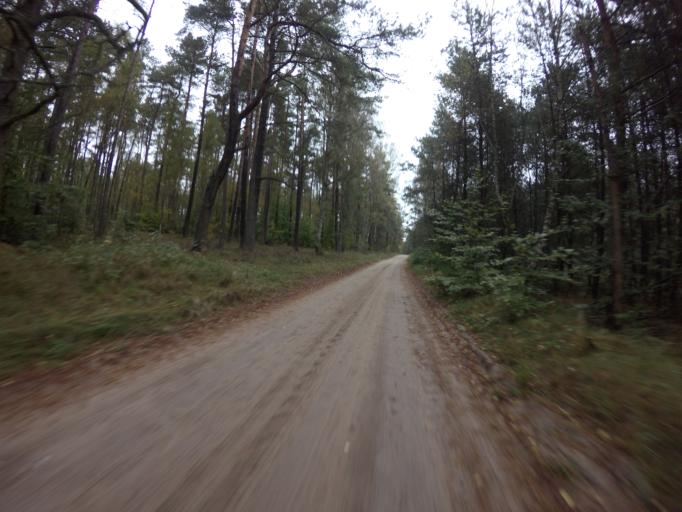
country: PL
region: Pomeranian Voivodeship
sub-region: Powiat kartuski
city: Stezyca
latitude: 54.1587
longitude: 17.9193
